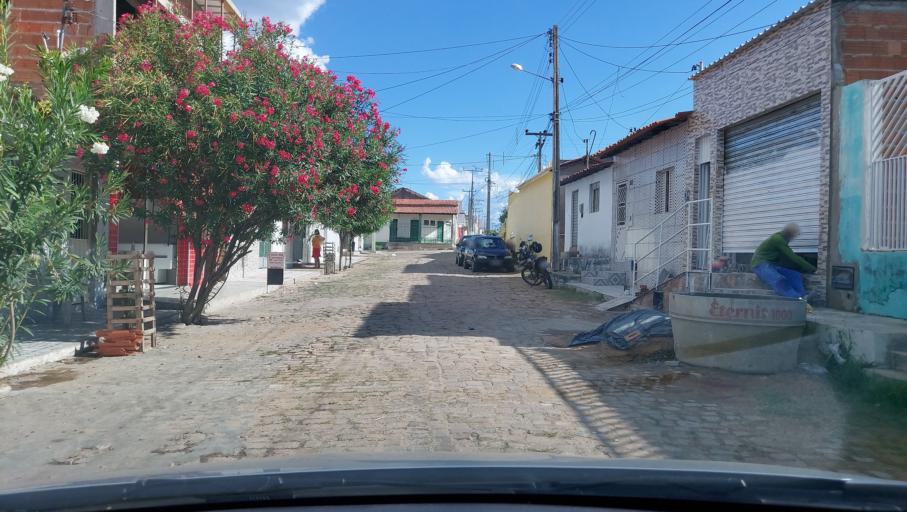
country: BR
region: Bahia
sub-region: Oliveira Dos Brejinhos
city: Beira Rio
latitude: -11.9973
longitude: -42.6266
